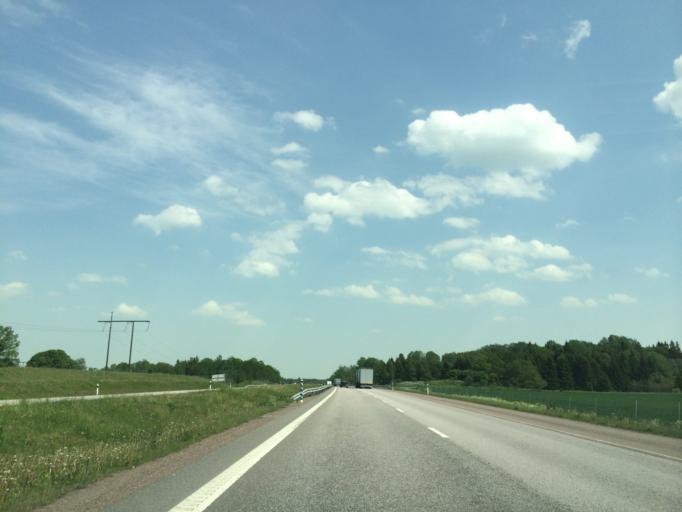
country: SE
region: OEstergoetland
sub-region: Boxholms Kommun
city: Boxholm
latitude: 58.3021
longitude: 14.9572
